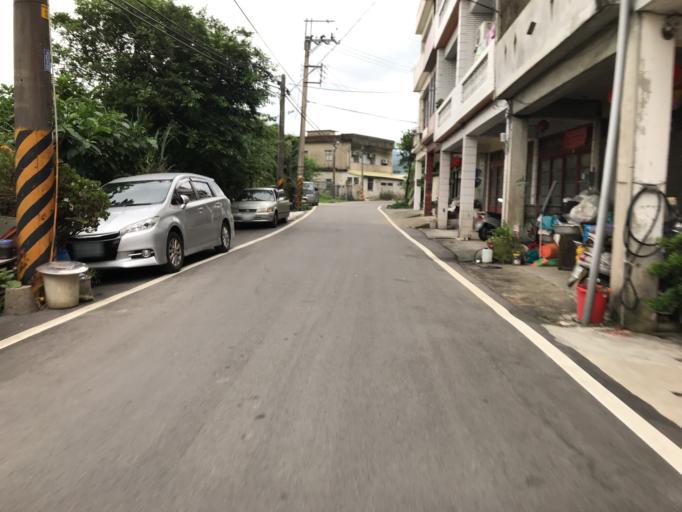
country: TW
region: Taiwan
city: Daxi
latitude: 24.7843
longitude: 121.1754
